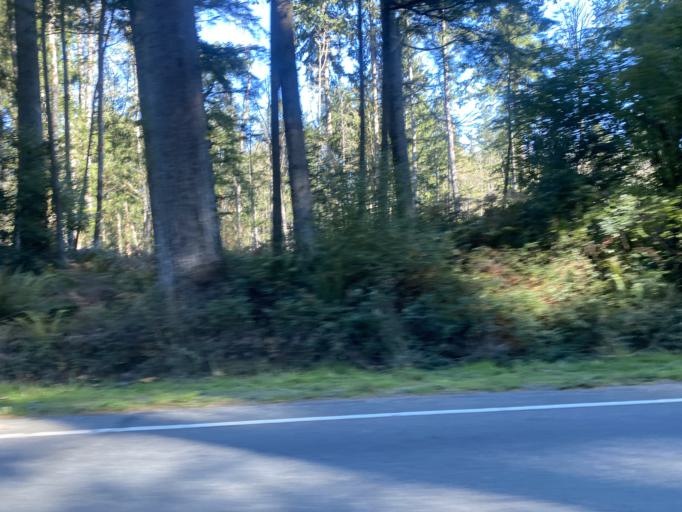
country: US
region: Washington
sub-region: Island County
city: Langley
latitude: 48.0171
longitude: -122.4270
